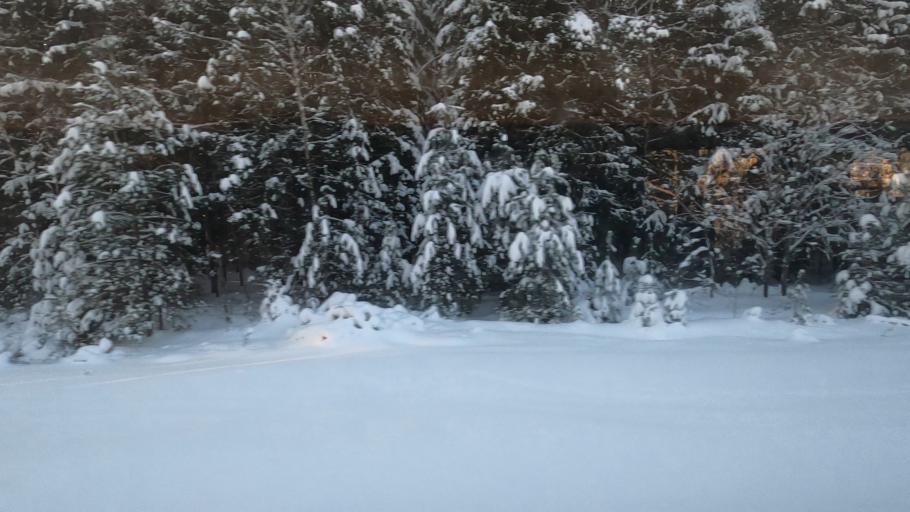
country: RU
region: Moskovskaya
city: Novo-Nikol'skoye
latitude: 56.5532
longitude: 37.5645
